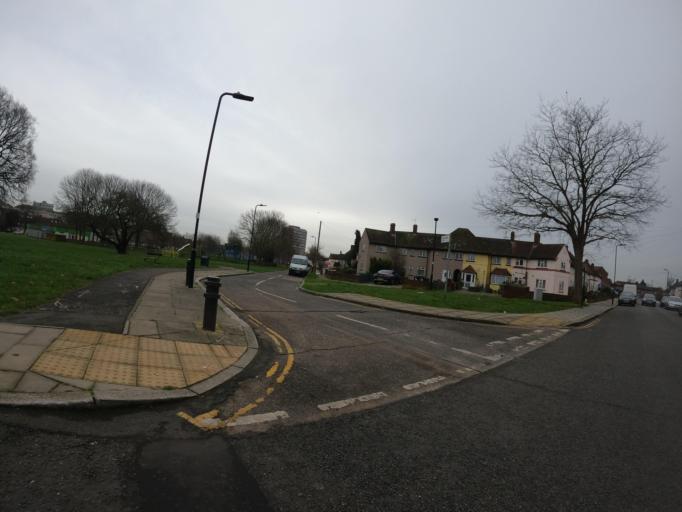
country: GB
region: England
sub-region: Greater London
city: Southall
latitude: 51.5178
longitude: -0.3623
